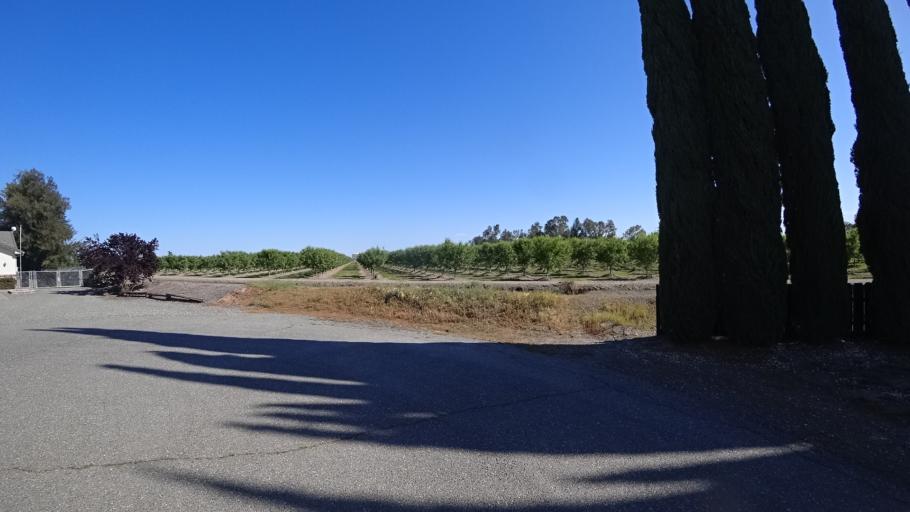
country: US
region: California
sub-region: Glenn County
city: Orland
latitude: 39.7308
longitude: -122.1654
